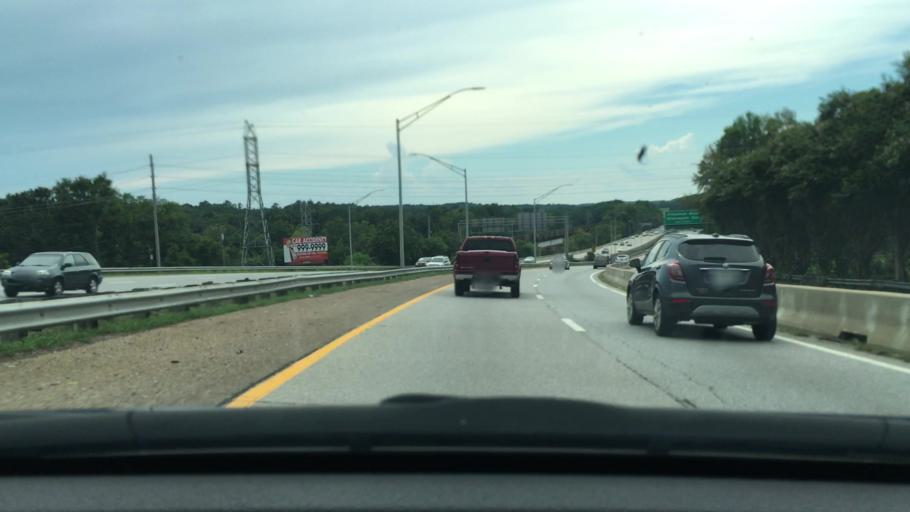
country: US
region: South Carolina
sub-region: Richland County
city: Columbia
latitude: 34.0085
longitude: -81.0561
